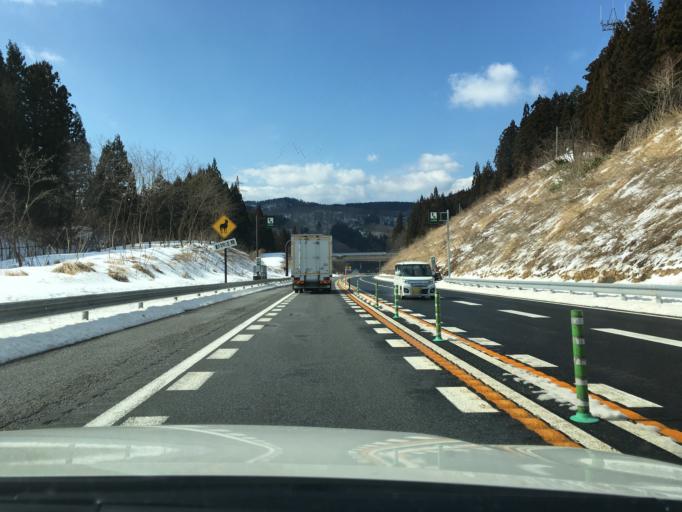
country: JP
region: Yamagata
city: Tsuruoka
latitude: 38.5892
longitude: 139.8916
